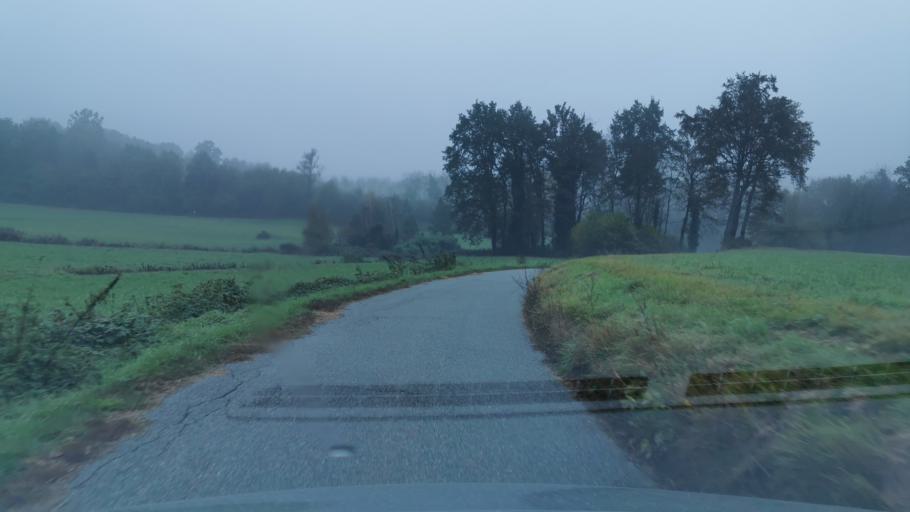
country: IT
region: Piedmont
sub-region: Provincia di Torino
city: Vialfre
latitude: 45.3760
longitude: 7.8144
